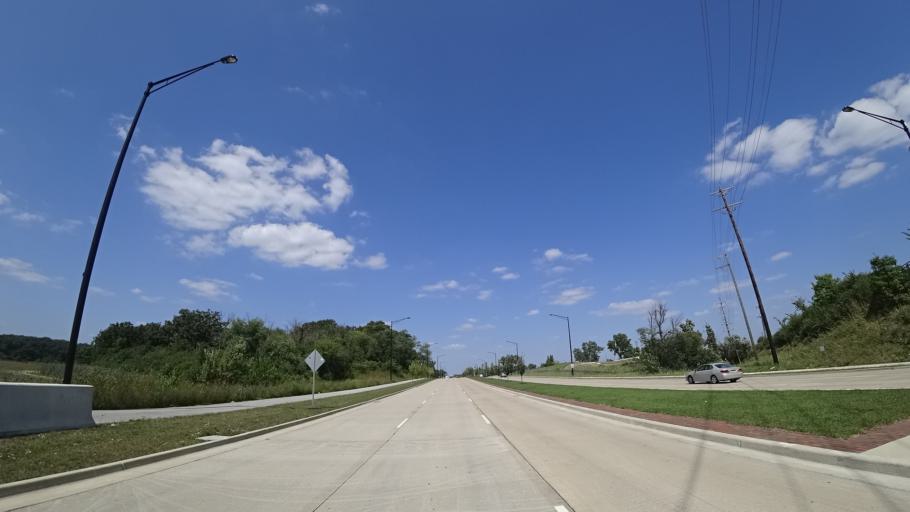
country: US
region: Illinois
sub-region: Cook County
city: Orland Park
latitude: 41.6365
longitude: -87.8540
